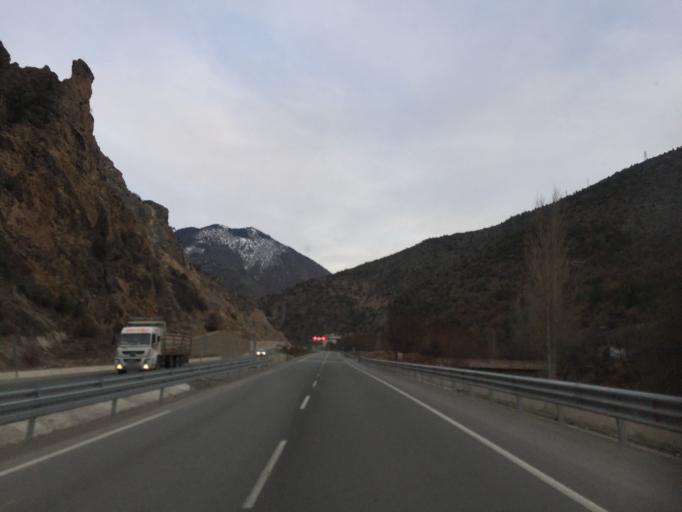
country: TR
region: Gumushane
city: Gumushkhane
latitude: 40.5213
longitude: 39.4037
